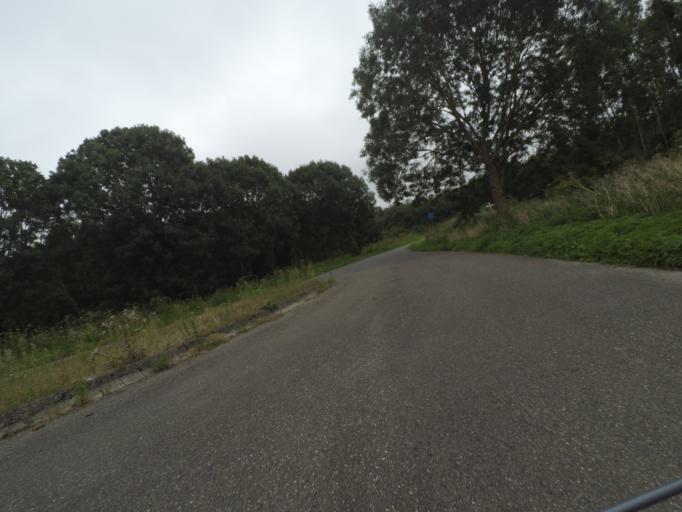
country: NL
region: Flevoland
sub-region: Gemeente Lelystad
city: Lelystad
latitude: 52.4306
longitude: 5.4016
